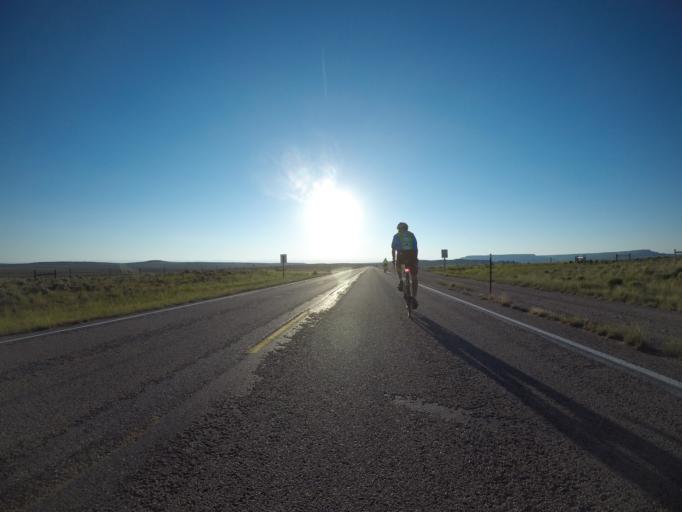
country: US
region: Wyoming
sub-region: Sublette County
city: Marbleton
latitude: 42.5797
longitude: -110.0003
